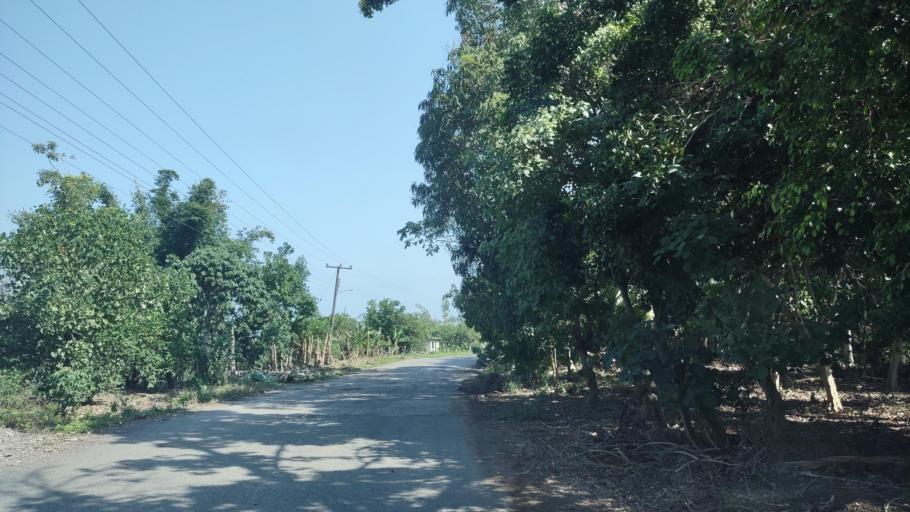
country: MX
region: Puebla
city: Espinal
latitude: 20.2540
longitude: -97.3330
